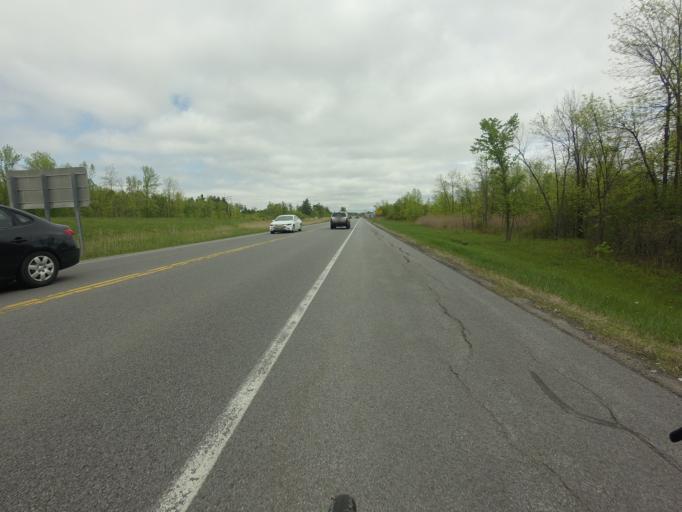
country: CA
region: Ontario
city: Cornwall
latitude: 44.9799
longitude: -74.7285
